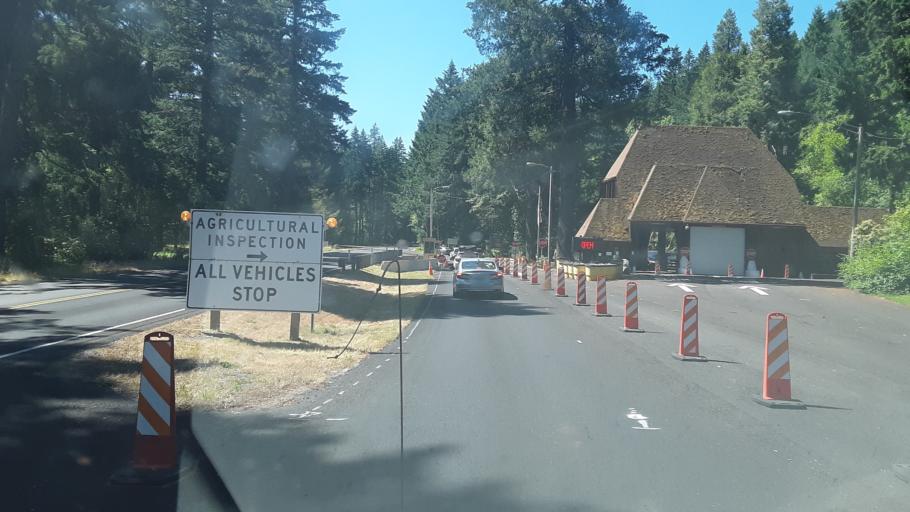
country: US
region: Oregon
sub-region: Josephine County
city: Cave Junction
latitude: 41.9888
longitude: -123.7180
